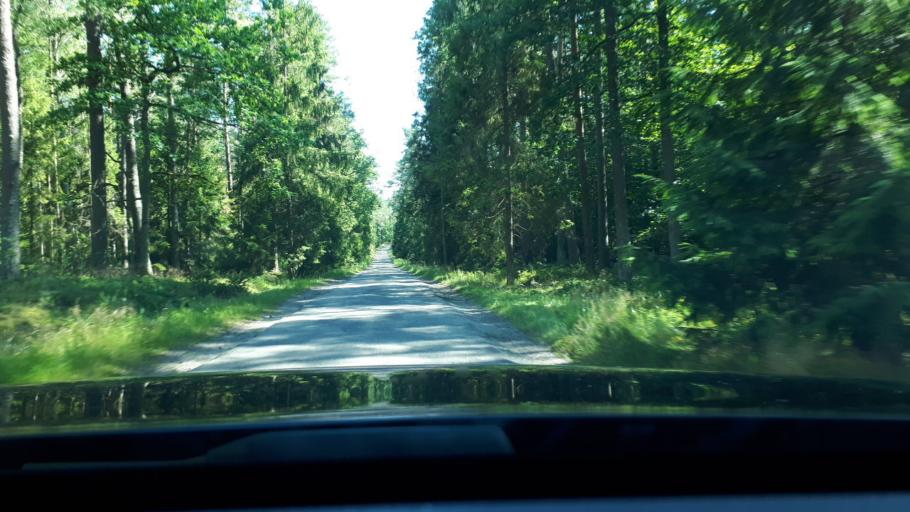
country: PL
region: Warmian-Masurian Voivodeship
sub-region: Powiat olsztynski
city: Stawiguda
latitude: 53.5863
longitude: 20.4501
